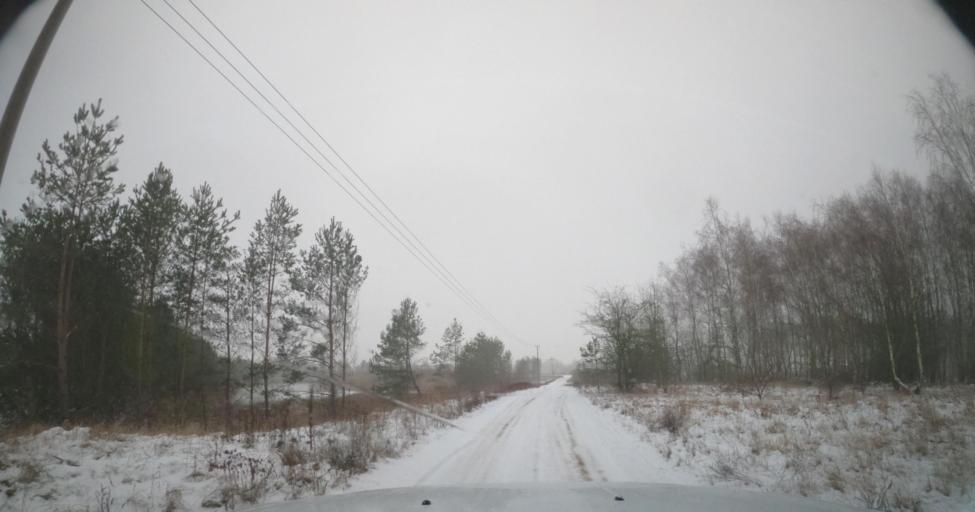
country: PL
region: West Pomeranian Voivodeship
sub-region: Powiat kamienski
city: Golczewo
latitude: 53.7797
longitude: 14.9565
